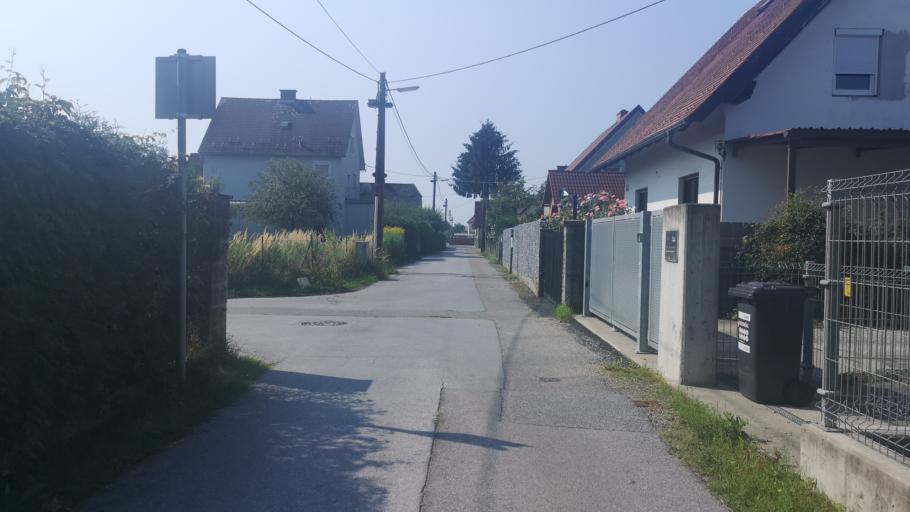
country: AT
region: Styria
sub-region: Graz Stadt
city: Wetzelsdorf
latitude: 47.0269
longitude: 15.4078
